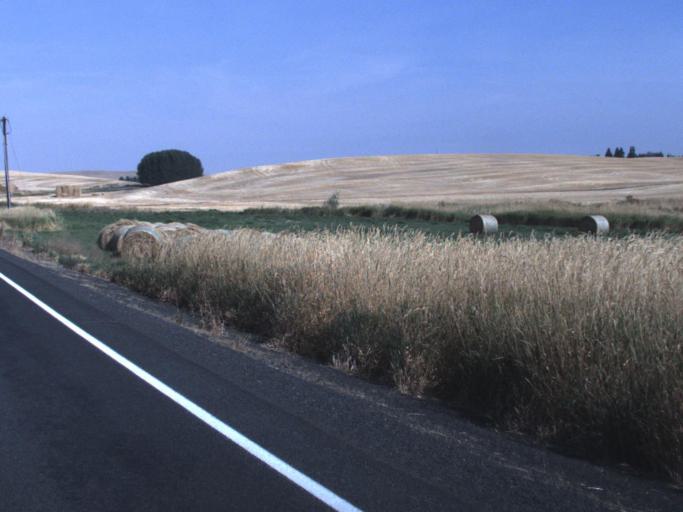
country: US
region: Washington
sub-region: Whitman County
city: Pullman
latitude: 46.8764
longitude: -117.1267
